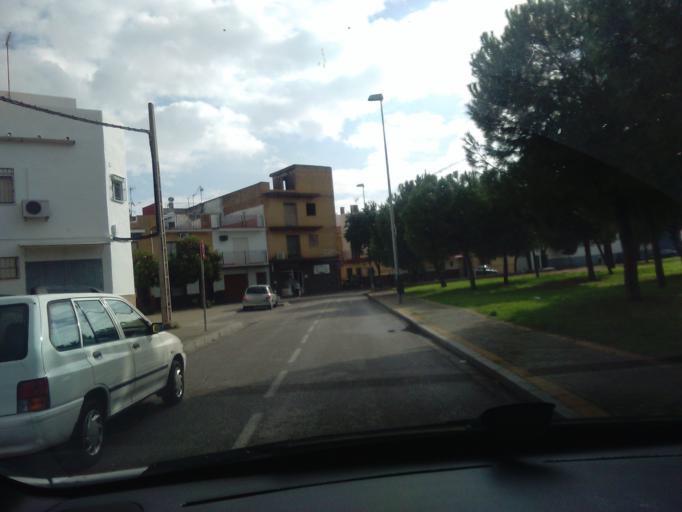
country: ES
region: Andalusia
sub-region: Provincia de Sevilla
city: Sevilla
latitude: 37.3825
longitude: -5.9133
